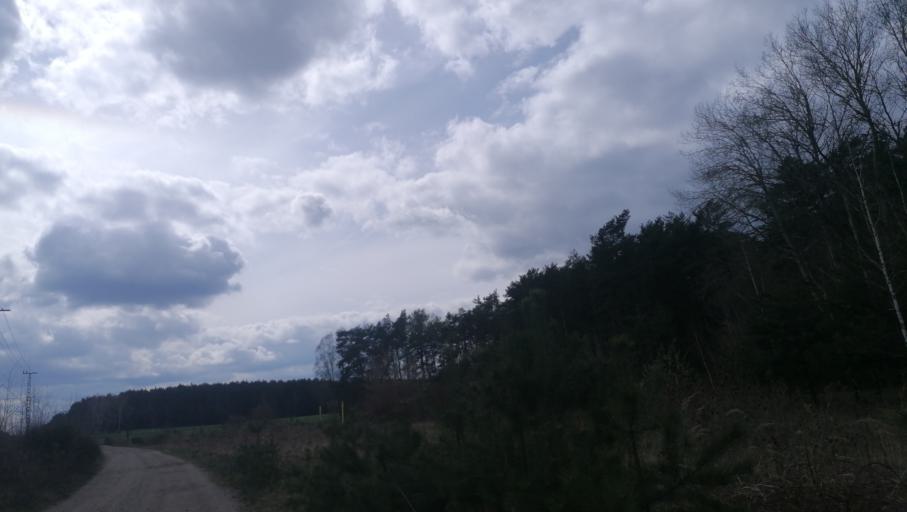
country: DE
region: Brandenburg
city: Cottbus
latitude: 51.6848
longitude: 14.3378
